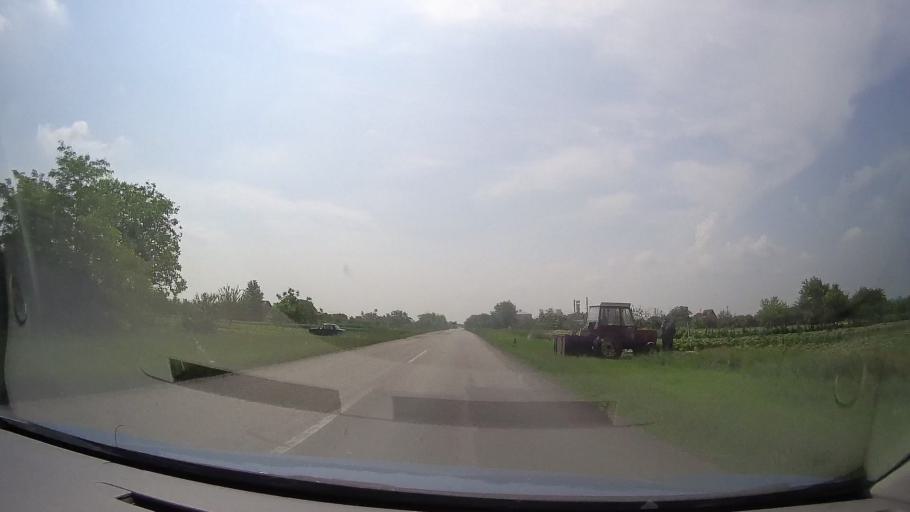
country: RS
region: Autonomna Pokrajina Vojvodina
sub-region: Juznobanatski Okrug
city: Kovacica
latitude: 45.0939
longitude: 20.6309
